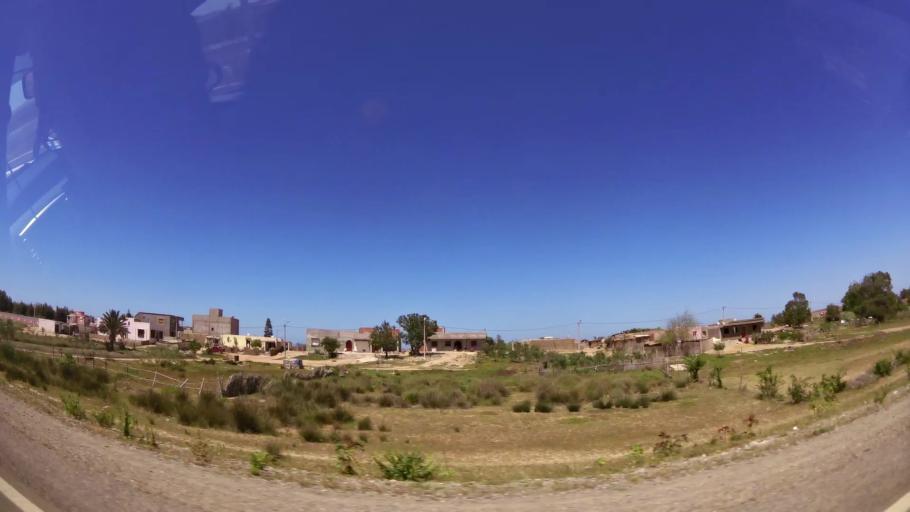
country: MA
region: Oriental
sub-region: Berkane-Taourirt
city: Madagh
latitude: 35.1016
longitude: -2.3363
